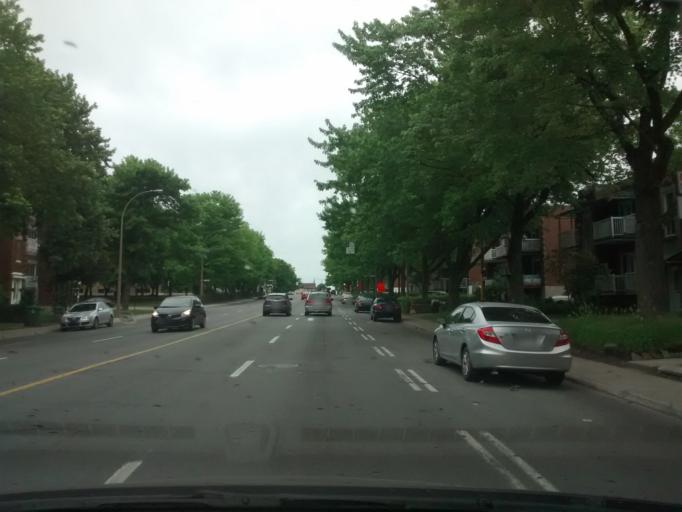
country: CA
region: Quebec
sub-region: Montreal
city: Saint-Leonard
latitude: 45.5546
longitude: -73.5848
